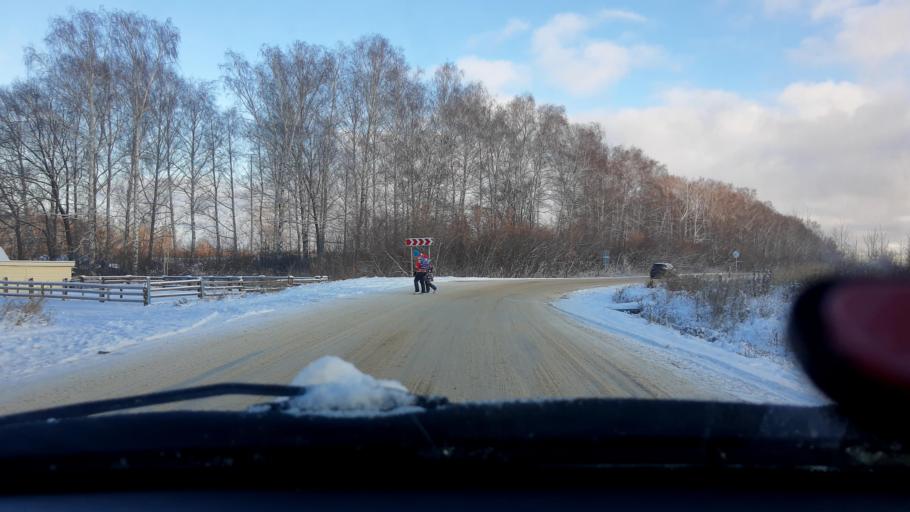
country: RU
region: Bashkortostan
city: Iglino
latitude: 54.8342
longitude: 56.4400
